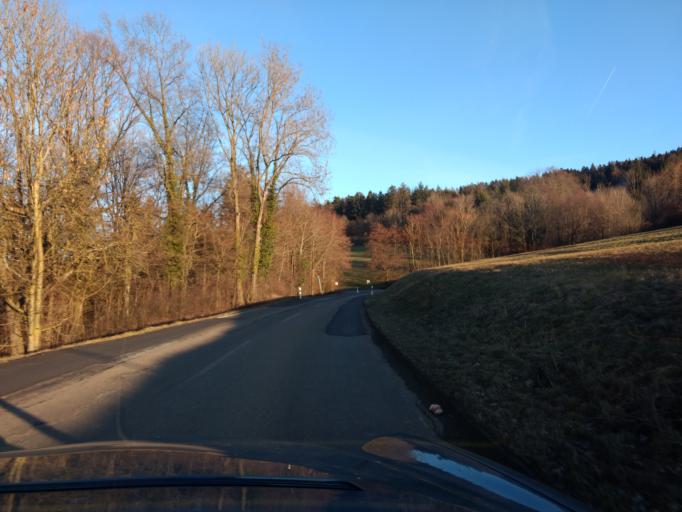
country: DE
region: Baden-Wuerttemberg
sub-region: Regierungsbezirk Stuttgart
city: Ottenbach
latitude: 48.7591
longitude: 9.7519
